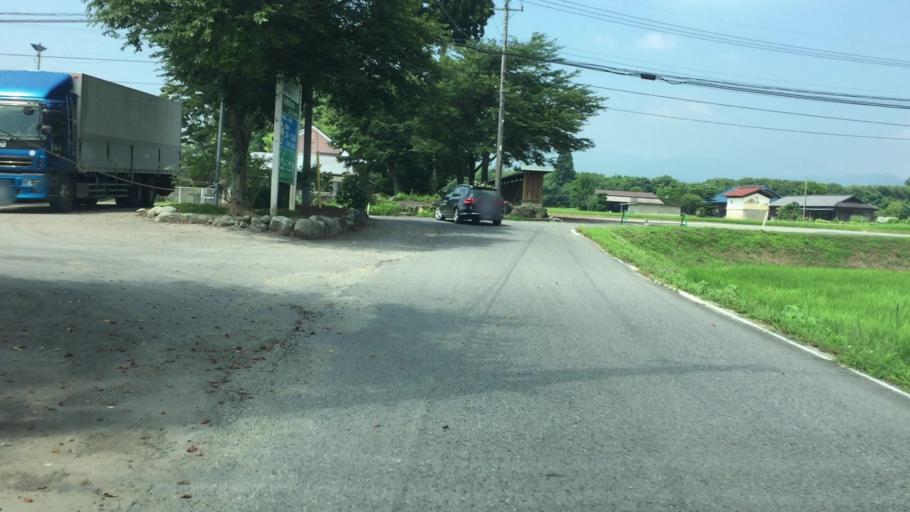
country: JP
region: Tochigi
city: Kuroiso
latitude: 36.9627
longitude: 139.9514
